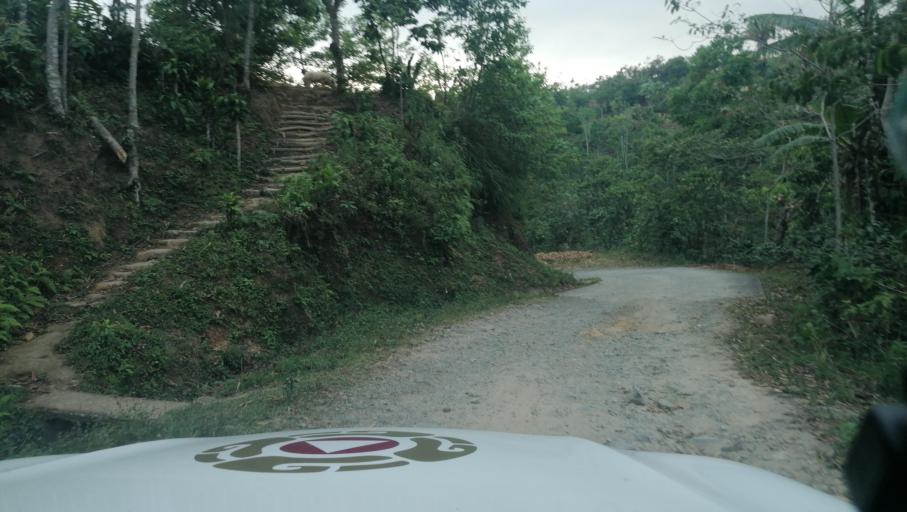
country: MX
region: Chiapas
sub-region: Cacahoatan
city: Benito Juarez
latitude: 15.1011
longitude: -92.2184
